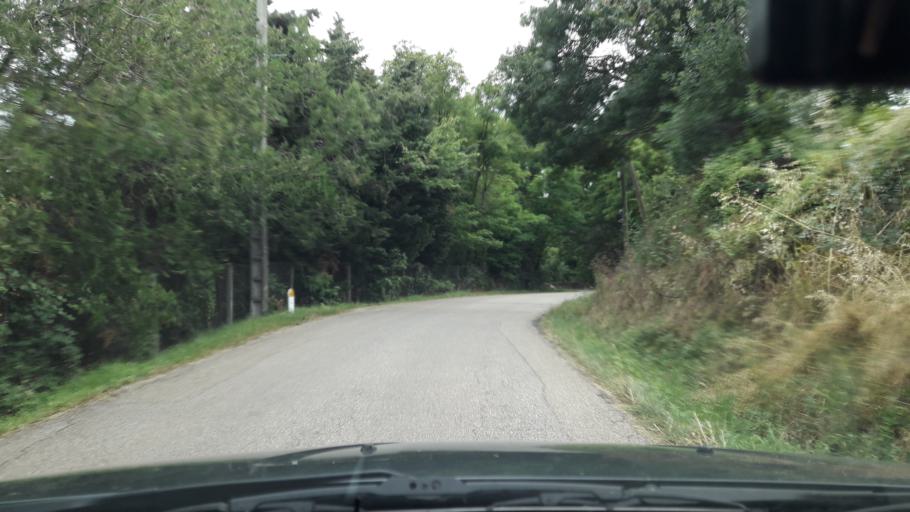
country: FR
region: Rhone-Alpes
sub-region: Departement de l'Ardeche
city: Alissas
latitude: 44.6882
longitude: 4.6324
